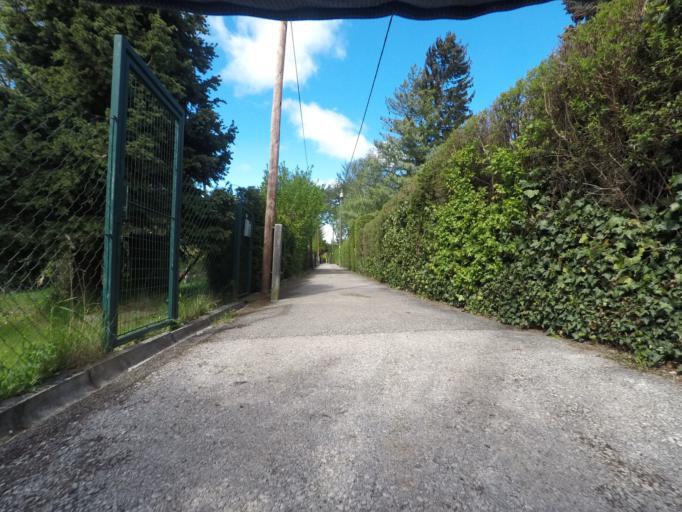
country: AT
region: Lower Austria
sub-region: Politischer Bezirk Modling
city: Perchtoldsdorf
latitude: 48.1729
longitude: 16.2593
